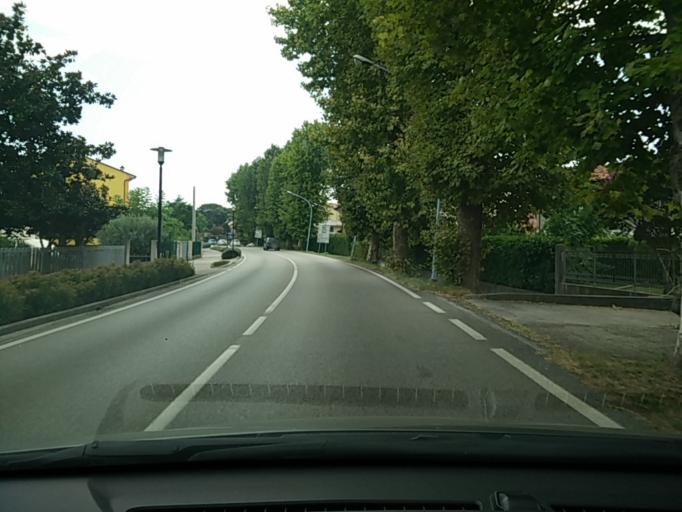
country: IT
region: Veneto
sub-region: Provincia di Venezia
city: Iesolo
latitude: 45.5403
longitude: 12.6478
